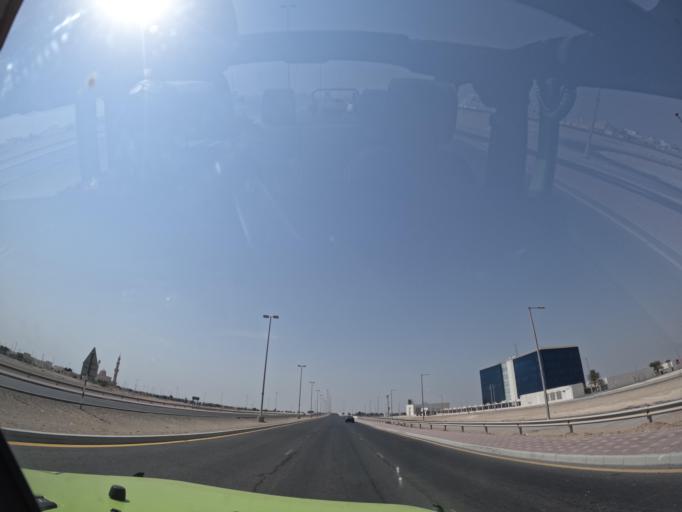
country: AE
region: Abu Dhabi
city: Abu Dhabi
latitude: 24.3368
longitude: 54.6417
